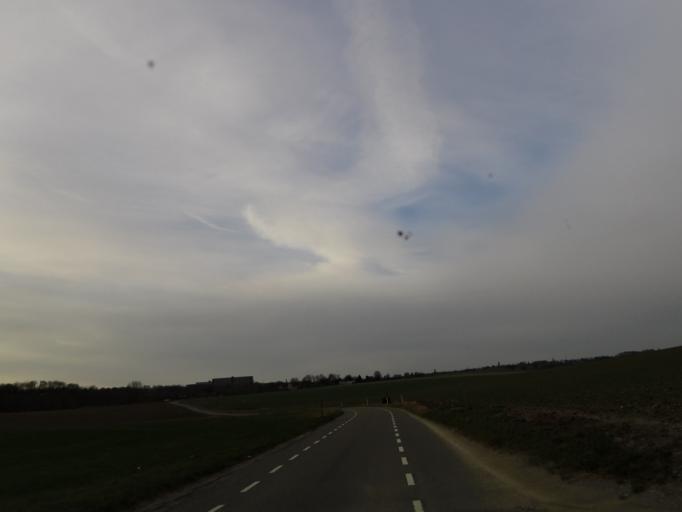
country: NL
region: Limburg
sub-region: Gemeente Onderbanken
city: Schinveld
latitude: 50.9641
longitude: 5.9667
